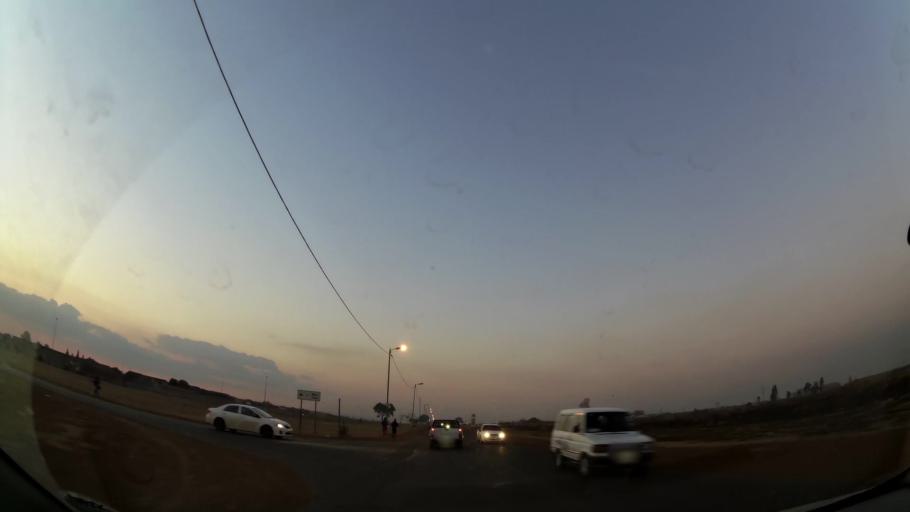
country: ZA
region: Gauteng
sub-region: Ekurhuleni Metropolitan Municipality
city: Springs
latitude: -26.3432
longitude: 28.3704
